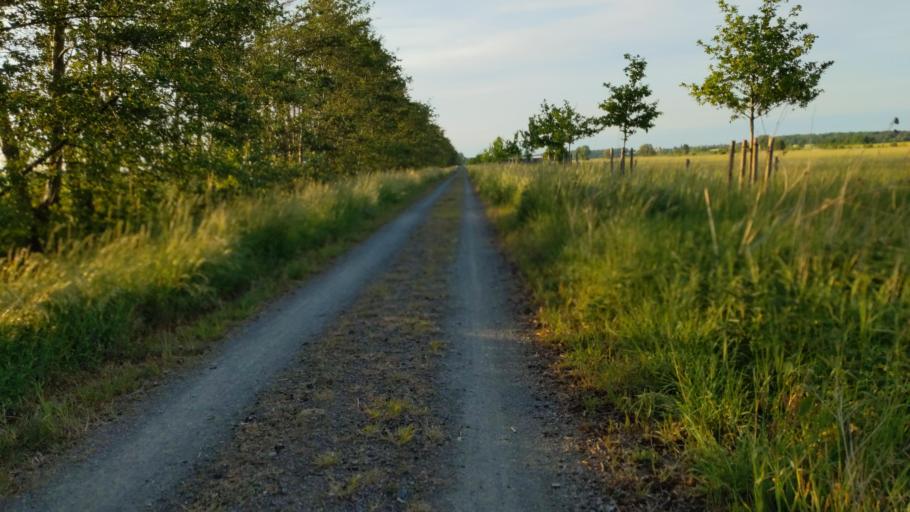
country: DE
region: Lower Saxony
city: Sickte
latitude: 52.2252
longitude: 10.5958
